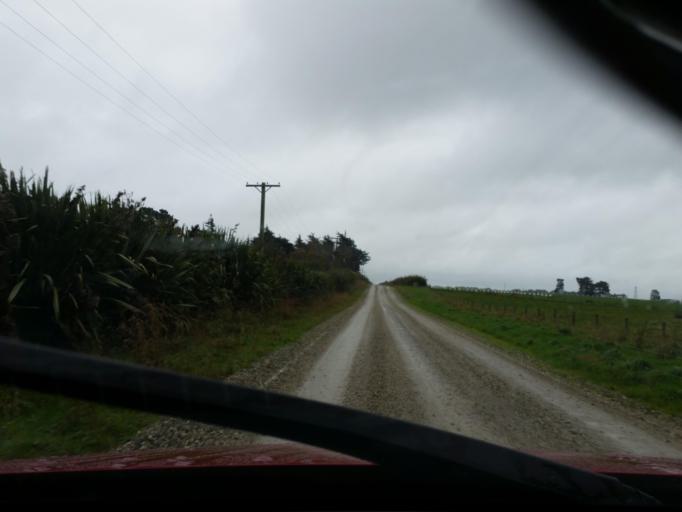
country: NZ
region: Southland
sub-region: Invercargill City
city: Invercargill
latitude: -46.2850
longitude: 168.5131
